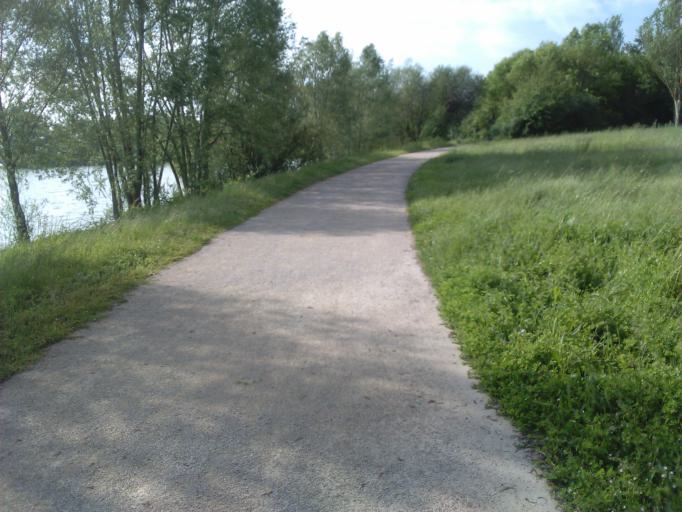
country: FR
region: Centre
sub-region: Departement du Loir-et-Cher
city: Villiers-sur-Loir
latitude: 47.7984
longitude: 0.9880
